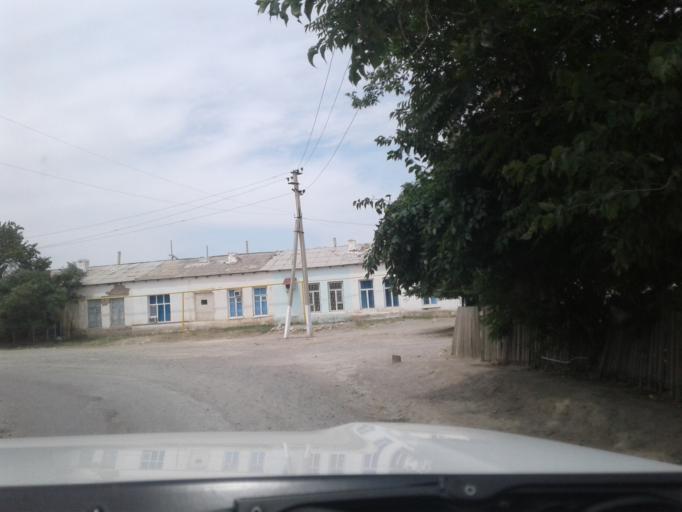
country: TM
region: Balkan
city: Serdar
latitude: 38.9840
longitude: 56.2770
